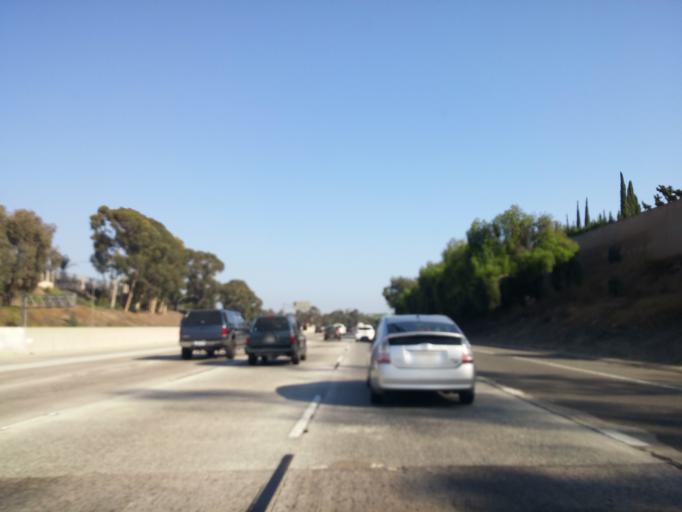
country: US
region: California
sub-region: Orange County
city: Mission Viejo
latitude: 33.6002
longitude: -117.6820
